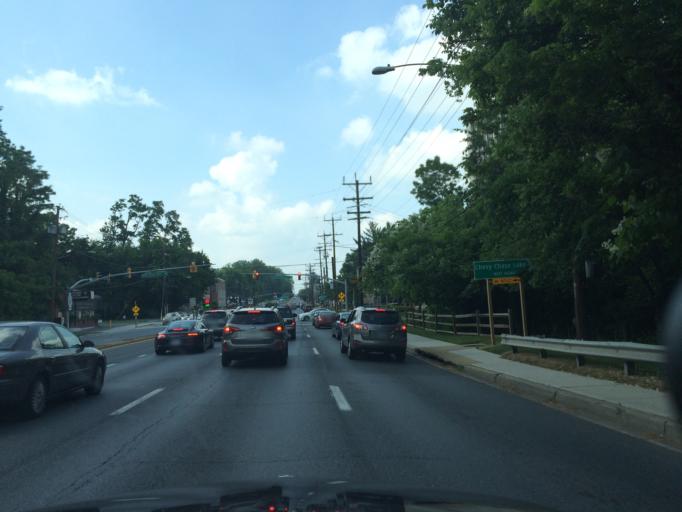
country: US
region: Maryland
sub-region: Montgomery County
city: Chevy Chase
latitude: 38.9932
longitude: -77.0771
